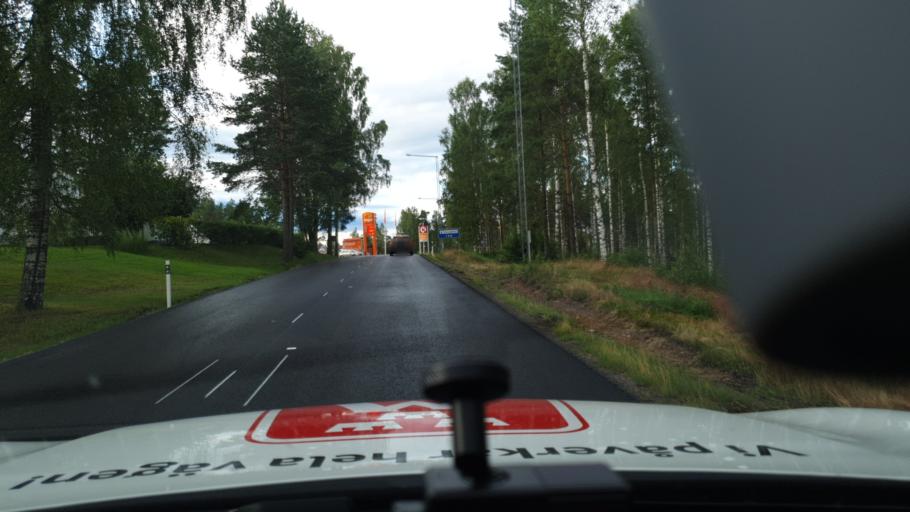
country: SE
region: Vaermland
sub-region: Torsby Kommun
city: Torsby
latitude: 60.2732
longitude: 13.0286
